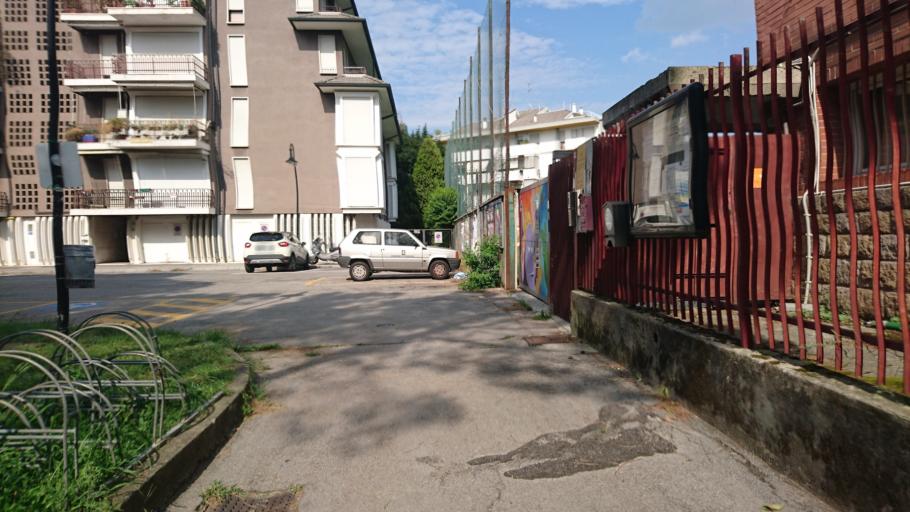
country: IT
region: Veneto
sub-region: Provincia di Padova
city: Padova
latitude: 45.4240
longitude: 11.8760
